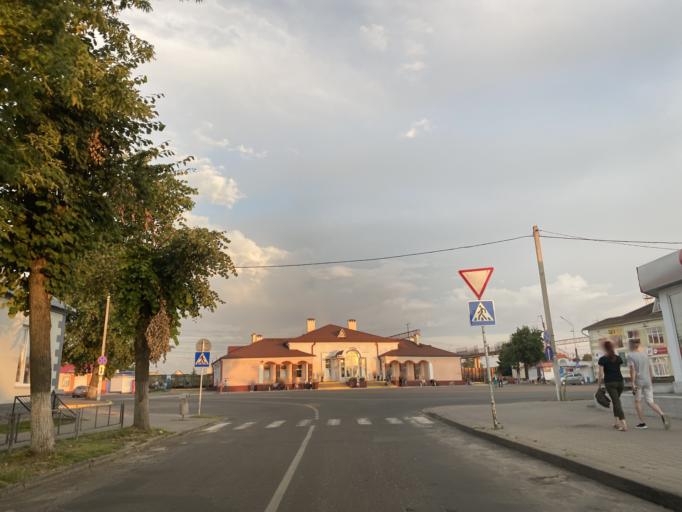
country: BY
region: Brest
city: Ivatsevichy
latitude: 52.7101
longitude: 25.3442
